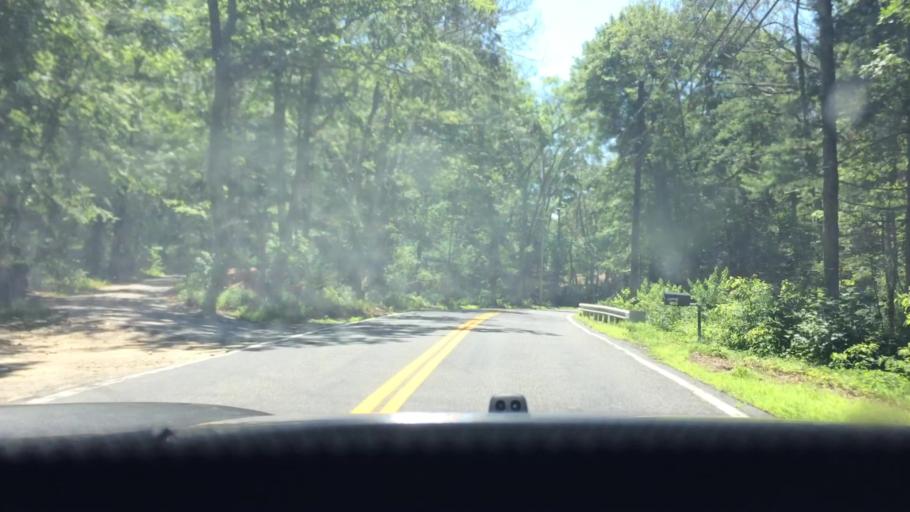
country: US
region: Rhode Island
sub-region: Providence County
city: Harrisville
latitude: 41.9964
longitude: -71.6820
